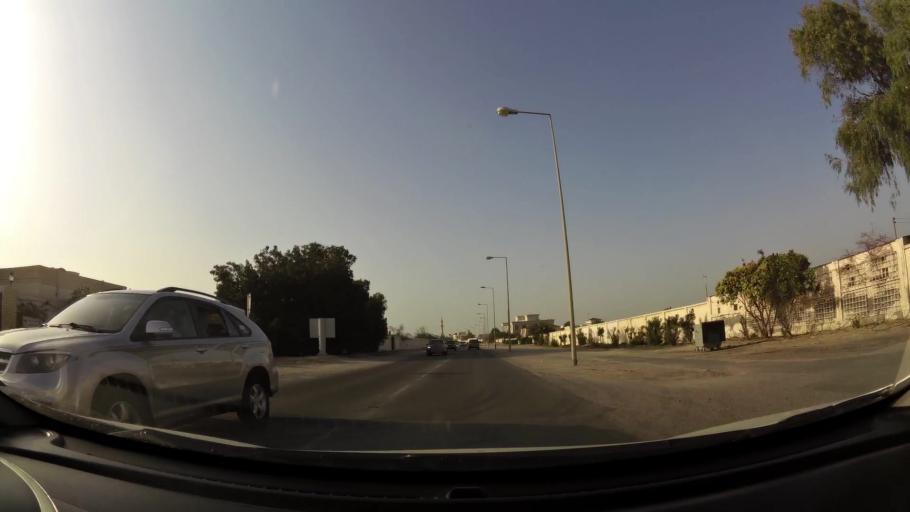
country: BH
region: Manama
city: Jidd Hafs
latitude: 26.2069
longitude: 50.4826
